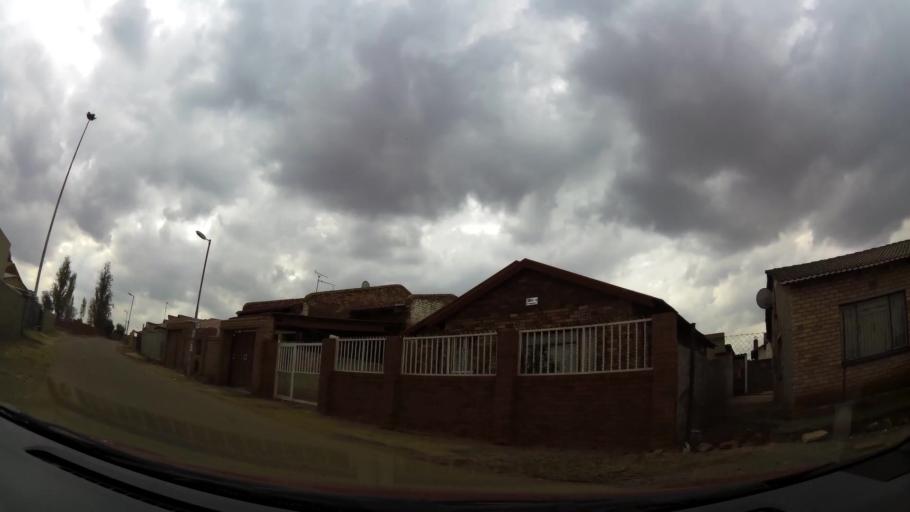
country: ZA
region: Gauteng
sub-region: City of Johannesburg Metropolitan Municipality
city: Soweto
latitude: -26.2591
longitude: 27.8421
